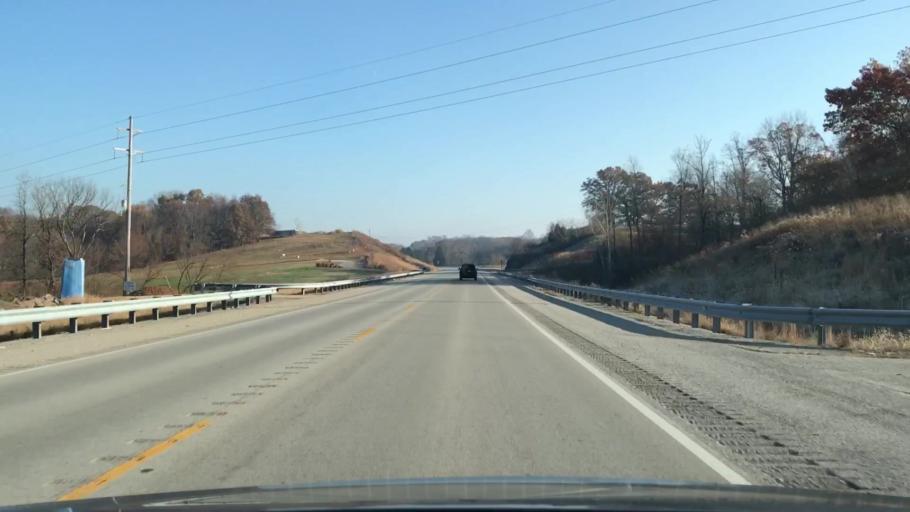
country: US
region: Kentucky
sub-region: Edmonson County
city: Brownsville
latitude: 37.1437
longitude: -86.2262
